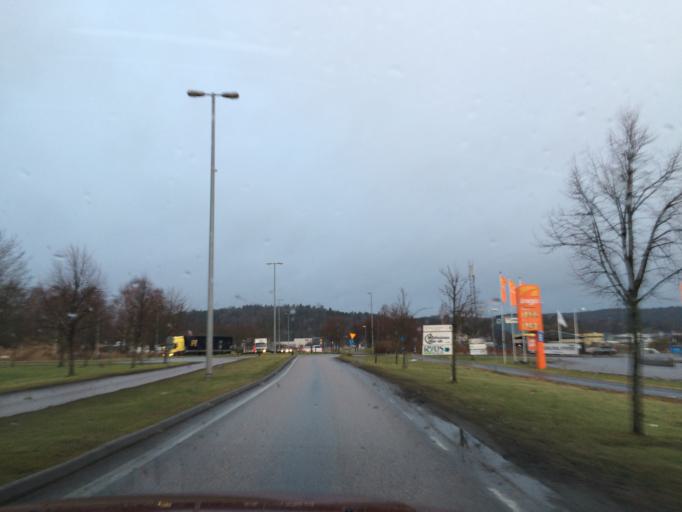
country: SE
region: Halland
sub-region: Kungsbacka Kommun
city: Kungsbacka
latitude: 57.5047
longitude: 12.0683
